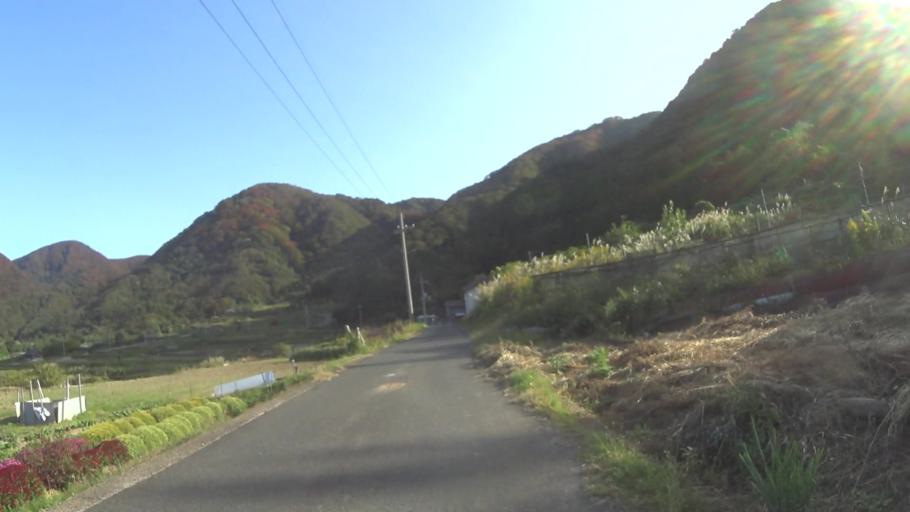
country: JP
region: Kyoto
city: Miyazu
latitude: 35.7631
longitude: 135.1994
